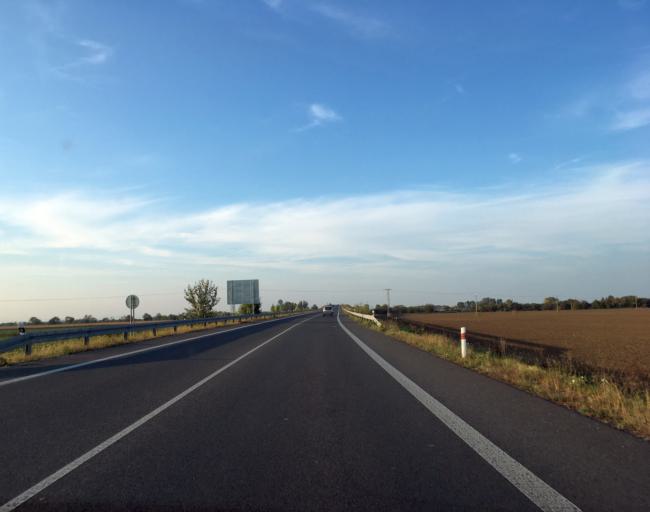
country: SK
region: Trnavsky
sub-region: Okres Galanta
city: Galanta
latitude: 48.1814
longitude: 17.7029
